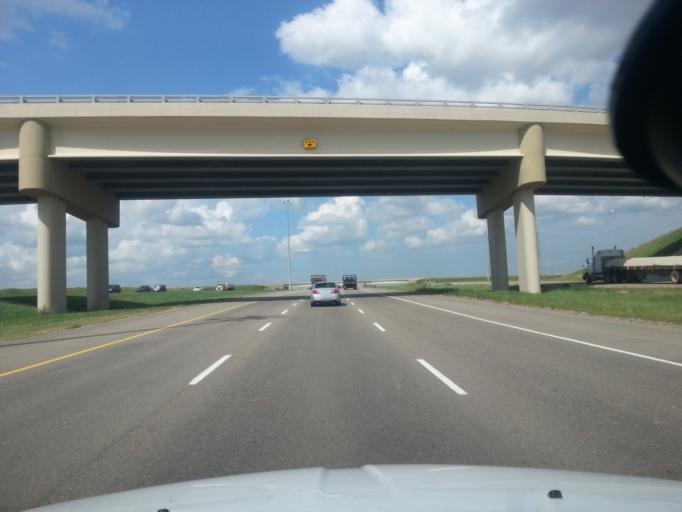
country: CA
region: Alberta
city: St. Albert
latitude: 53.5712
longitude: -113.6614
